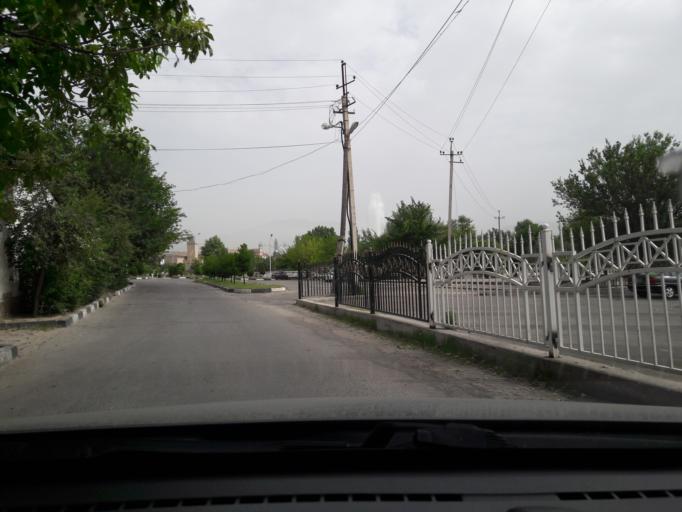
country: TJ
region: Dushanbe
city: Dushanbe
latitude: 38.5811
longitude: 68.7651
